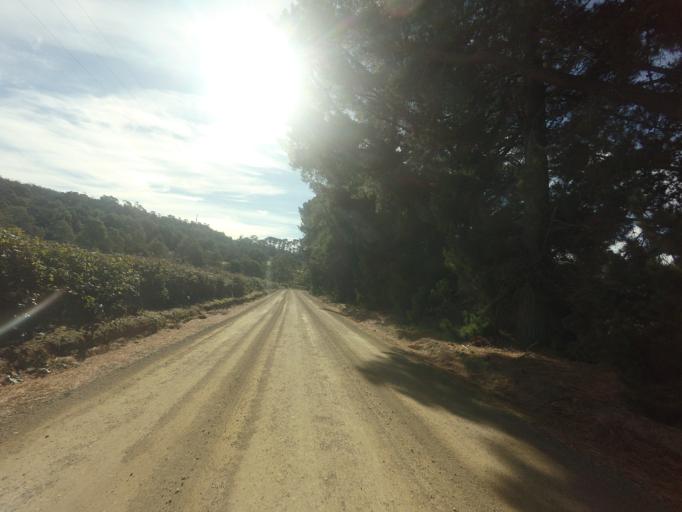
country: AU
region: Tasmania
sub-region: Clarence
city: Sandford
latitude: -43.1460
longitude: 147.7642
